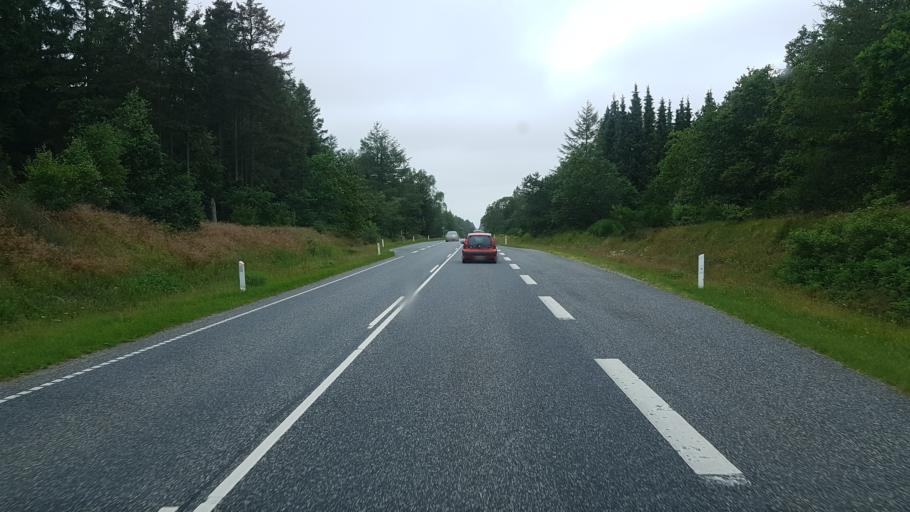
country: DK
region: Central Jutland
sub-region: Lemvig Kommune
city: Lemvig
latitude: 56.4543
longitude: 8.3418
